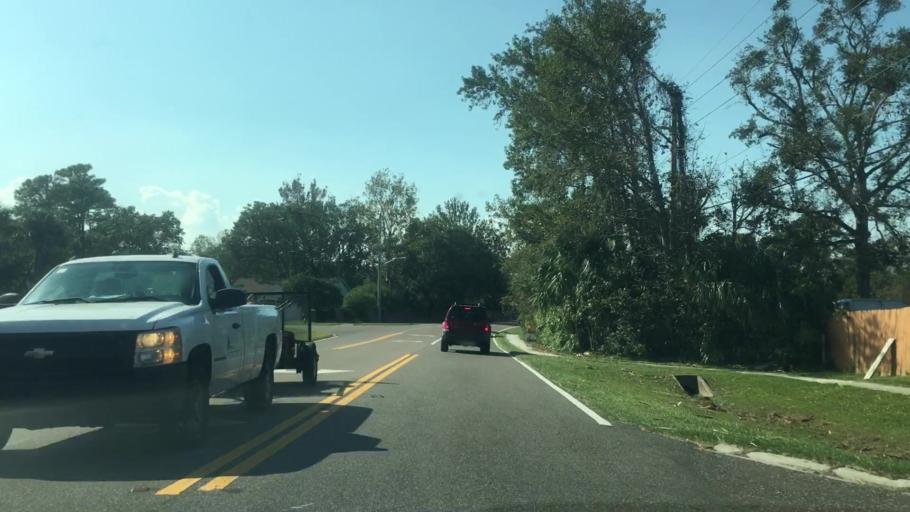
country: US
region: Florida
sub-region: Duval County
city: Neptune Beach
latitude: 30.3013
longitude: -81.4418
